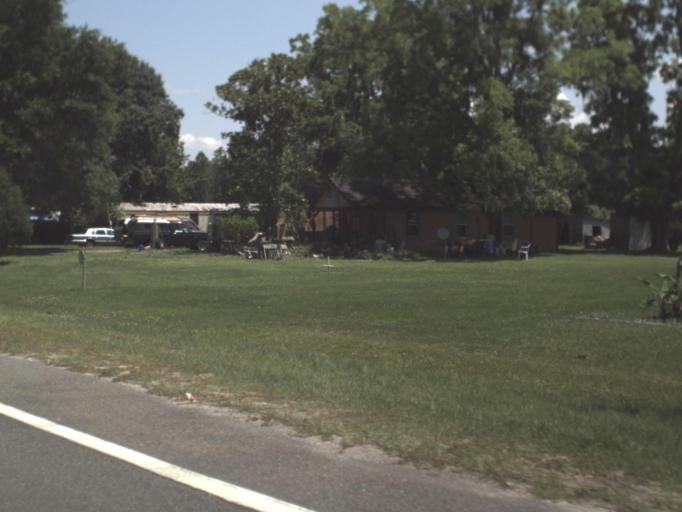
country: US
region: Florida
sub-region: Bradford County
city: Starke
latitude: 29.8969
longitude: -82.0873
